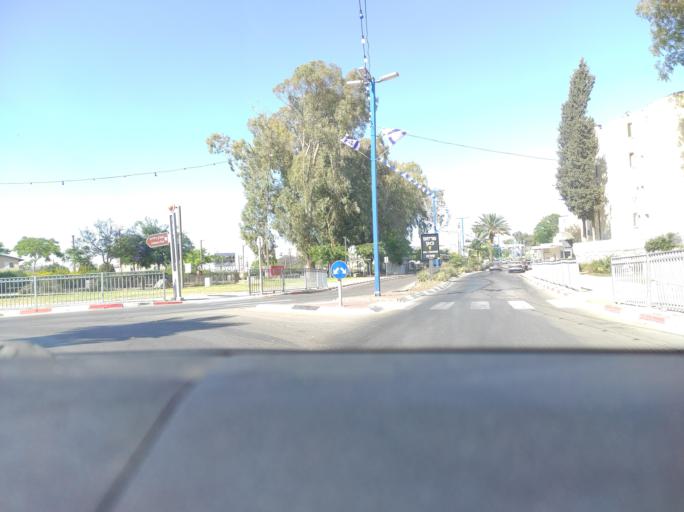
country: IL
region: Southern District
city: Sederot
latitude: 31.5257
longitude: 34.5967
